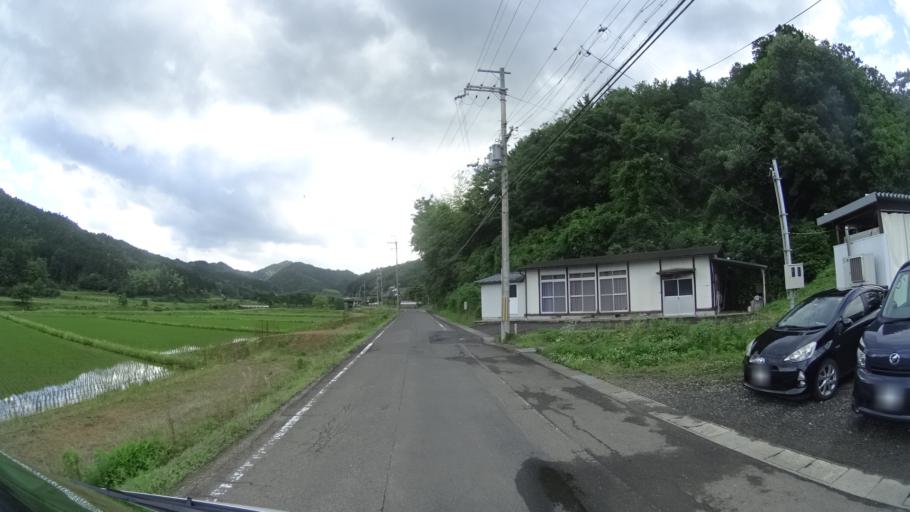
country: JP
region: Kyoto
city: Ayabe
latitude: 35.3769
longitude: 135.2317
